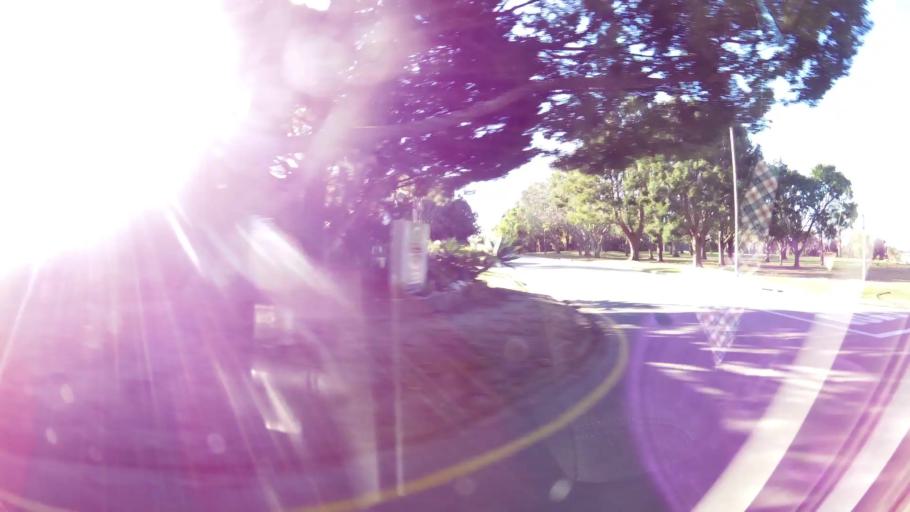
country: ZA
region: Western Cape
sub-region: Eden District Municipality
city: George
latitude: -33.9462
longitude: 22.4563
